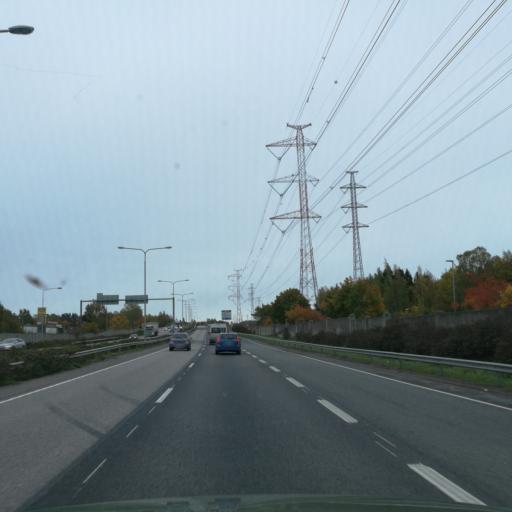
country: FI
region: Uusimaa
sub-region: Helsinki
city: Vantaa
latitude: 60.2829
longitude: 25.0262
